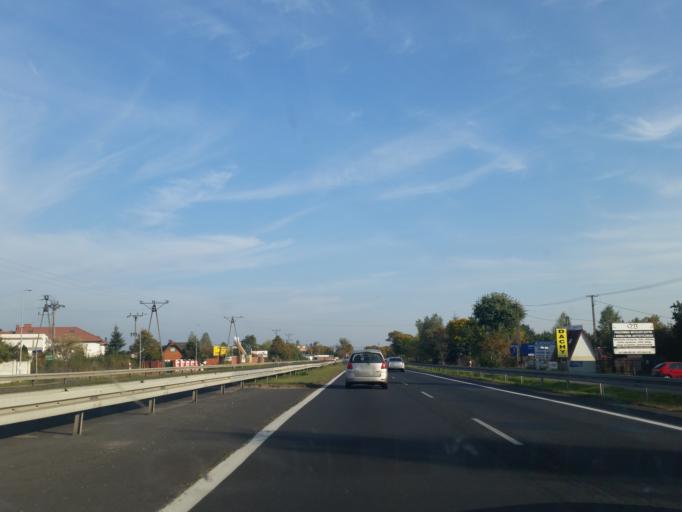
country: PL
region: Masovian Voivodeship
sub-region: Powiat warszawski zachodni
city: Dziekanow Lesny
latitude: 52.3524
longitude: 20.8513
